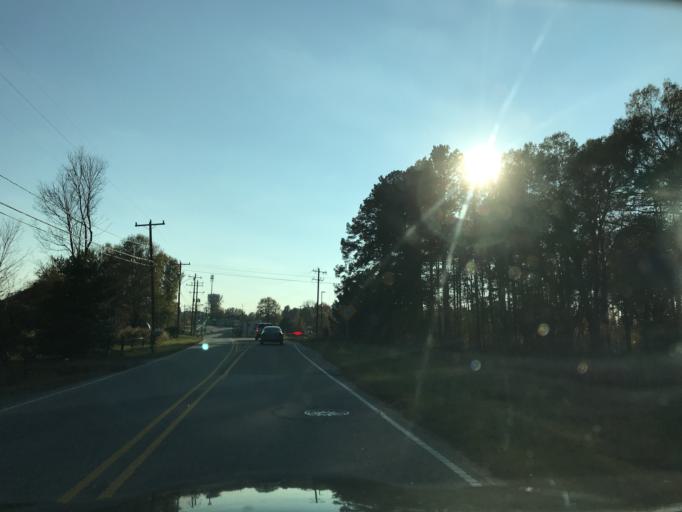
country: US
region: North Carolina
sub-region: Granville County
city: Creedmoor
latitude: 36.1243
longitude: -78.6848
